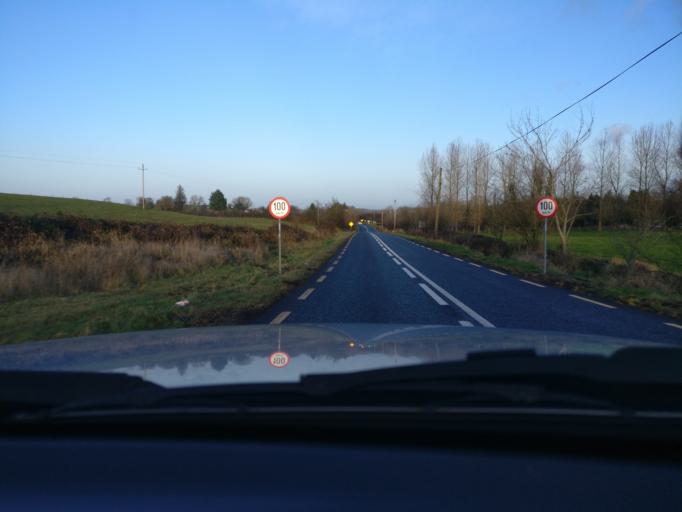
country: IE
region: Leinster
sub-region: An Mhi
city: Navan
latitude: 53.7981
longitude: -6.6798
